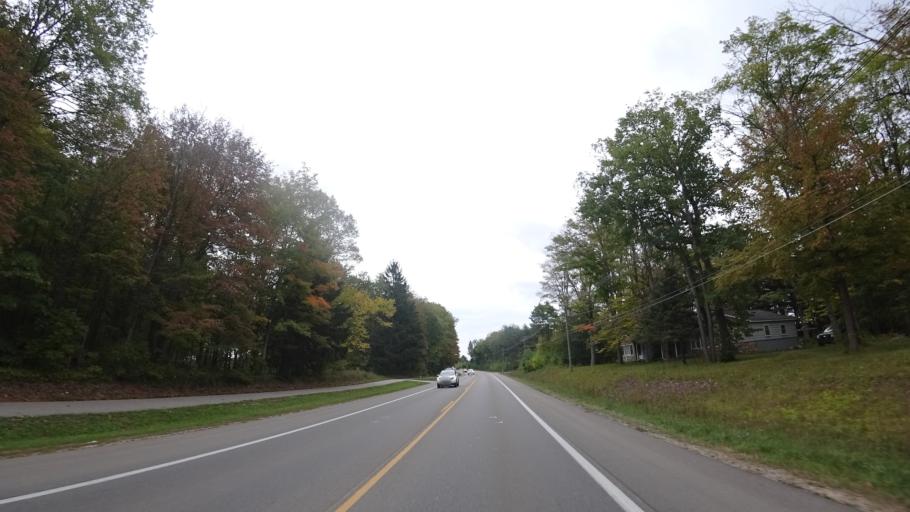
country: US
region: Michigan
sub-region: Emmet County
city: Petoskey
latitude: 45.4284
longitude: -84.9203
